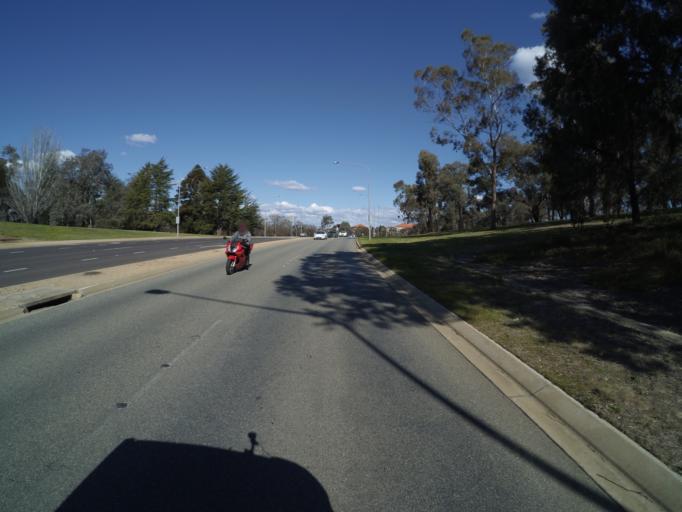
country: AU
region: Australian Capital Territory
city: Forrest
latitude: -35.3056
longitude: 149.1284
